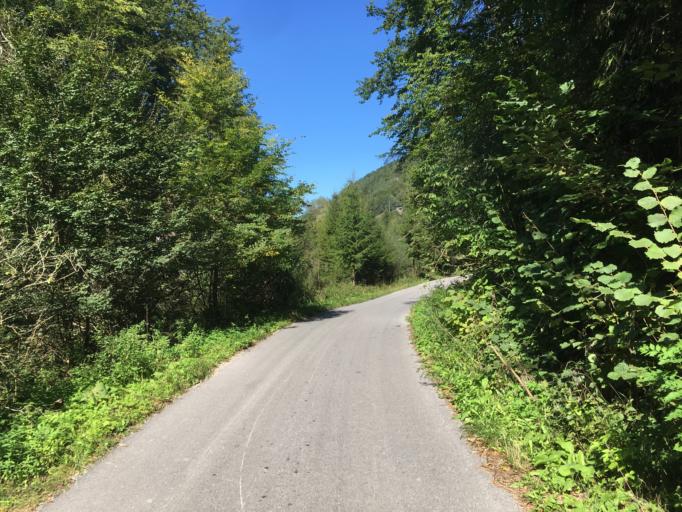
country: SK
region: Trenciansky
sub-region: Okres Povazska Bystrica
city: Povazska Bystrica
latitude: 49.0156
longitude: 18.4404
